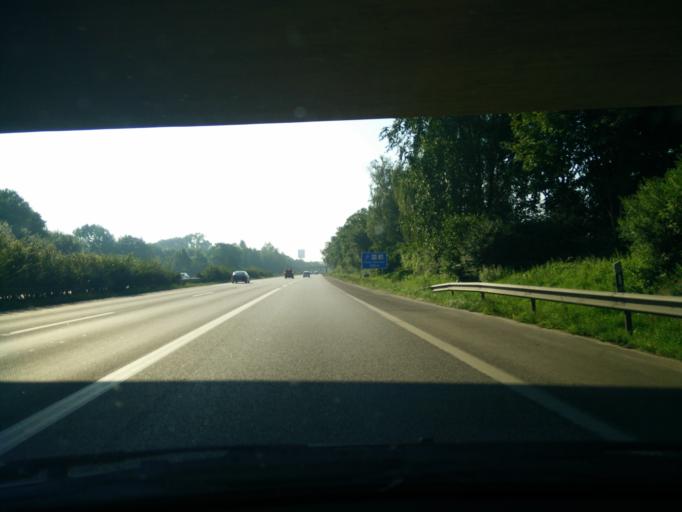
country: DE
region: Schleswig-Holstein
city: Ellerhoop
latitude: 53.7168
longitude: 9.7554
